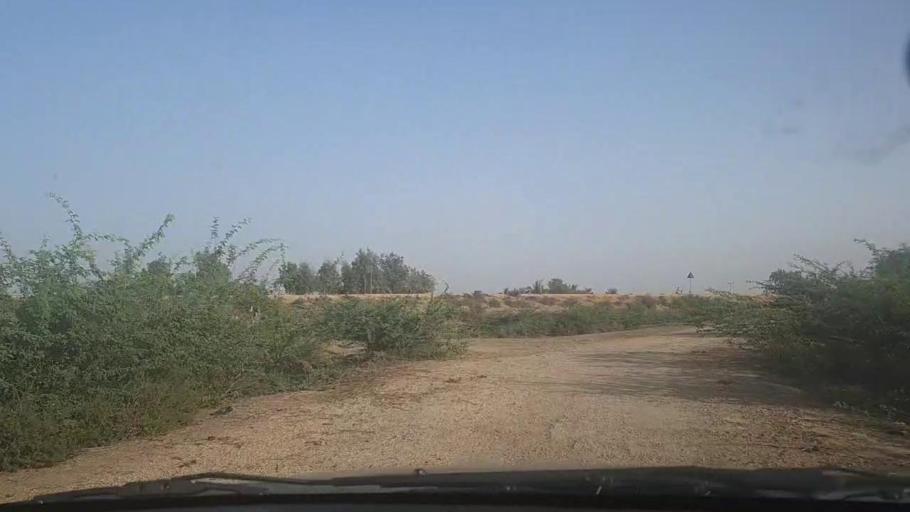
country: PK
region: Sindh
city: Keti Bandar
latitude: 24.2903
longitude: 67.6153
